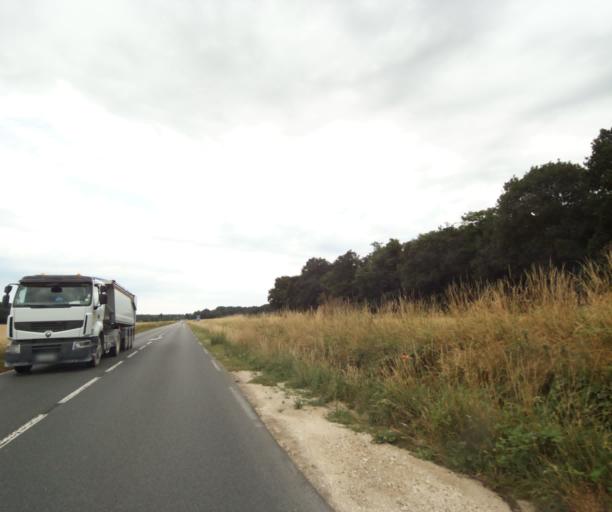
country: FR
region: Ile-de-France
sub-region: Departement de Seine-et-Marne
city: Cely
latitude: 48.4512
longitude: 2.5081
